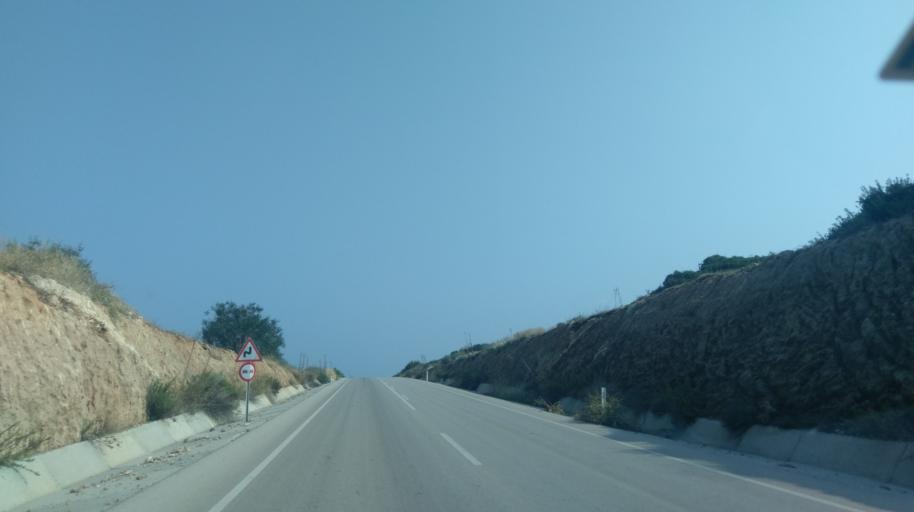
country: CY
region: Ammochostos
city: Trikomo
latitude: 35.4240
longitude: 33.8904
